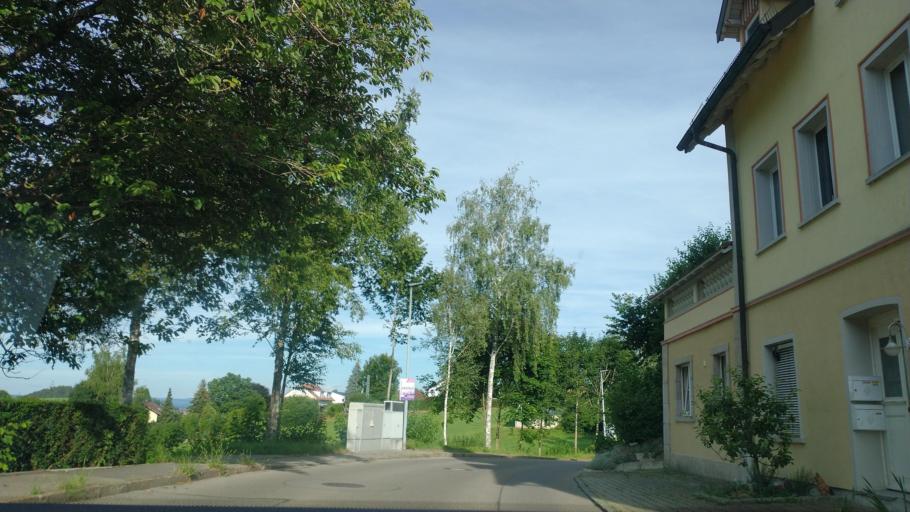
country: DE
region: Baden-Wuerttemberg
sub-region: Tuebingen Region
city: Neukirch
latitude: 47.6600
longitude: 9.7005
